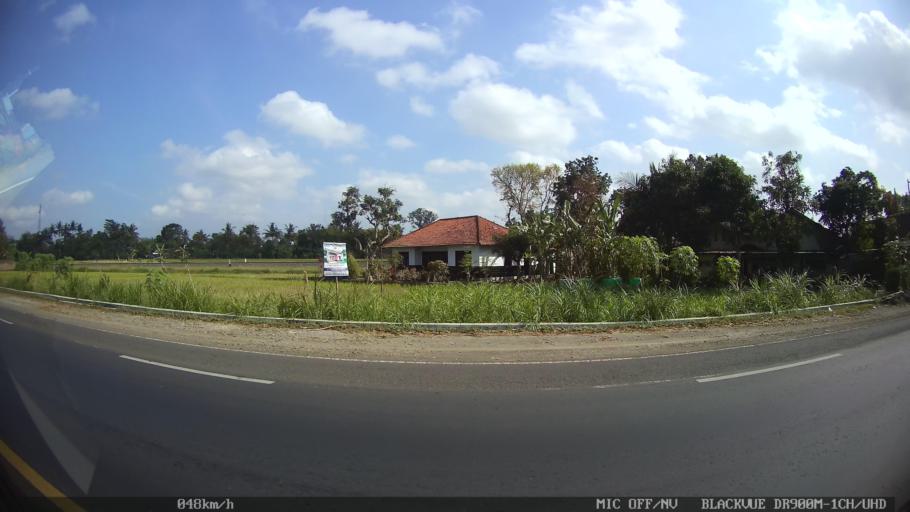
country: ID
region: Daerah Istimewa Yogyakarta
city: Godean
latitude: -7.8247
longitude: 110.2306
